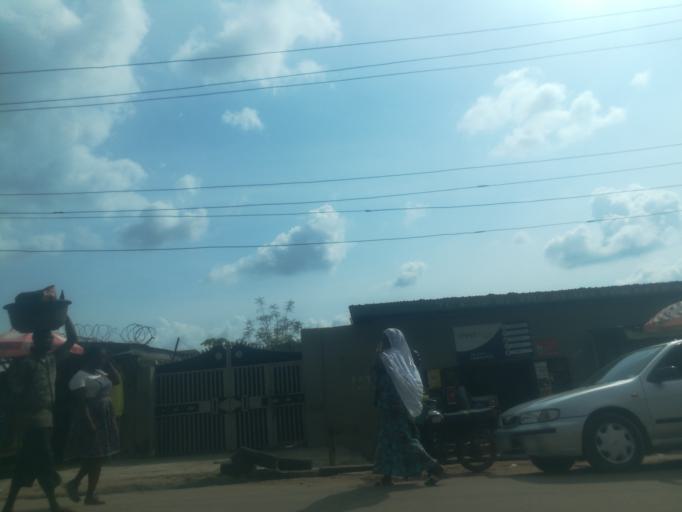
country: NG
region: Oyo
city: Ibadan
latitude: 7.3835
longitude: 3.8271
